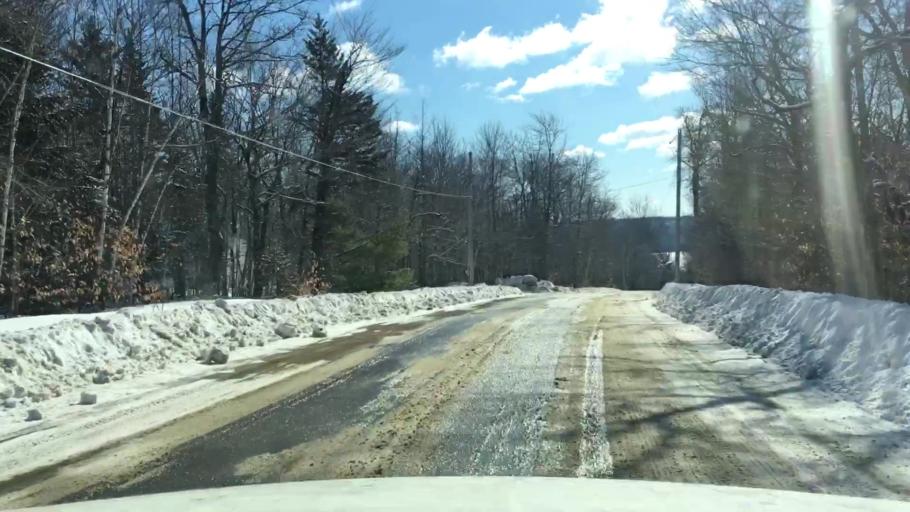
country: US
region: Maine
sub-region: Washington County
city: Calais
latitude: 45.0773
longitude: -67.5044
